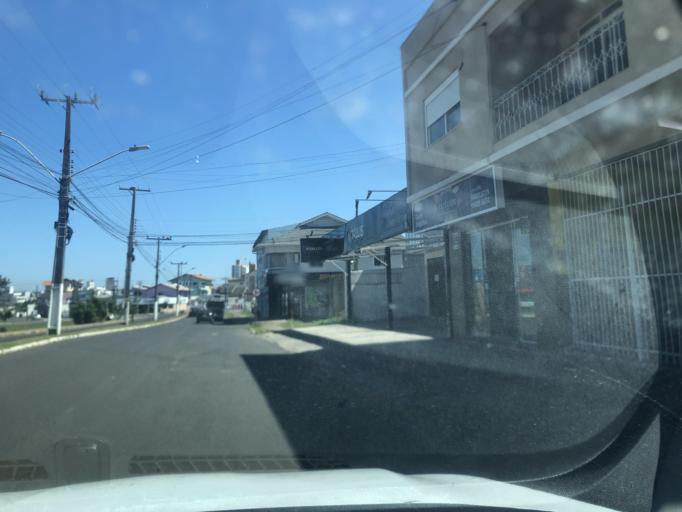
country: BR
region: Santa Catarina
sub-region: Lages
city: Lages
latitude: -27.8204
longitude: -50.3134
